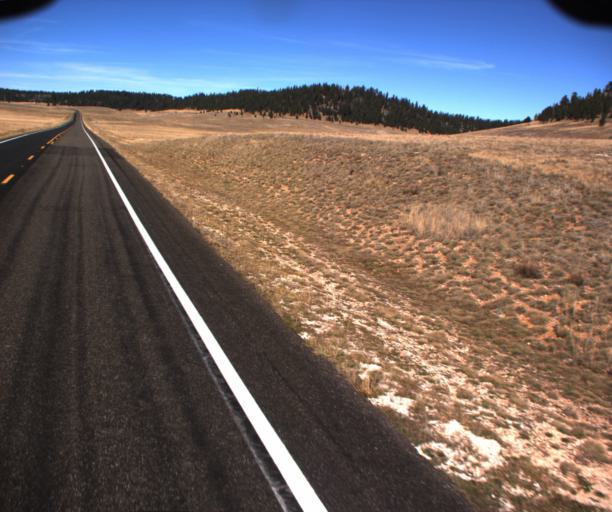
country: US
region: Arizona
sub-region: Coconino County
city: Grand Canyon
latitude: 36.4818
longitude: -112.1275
